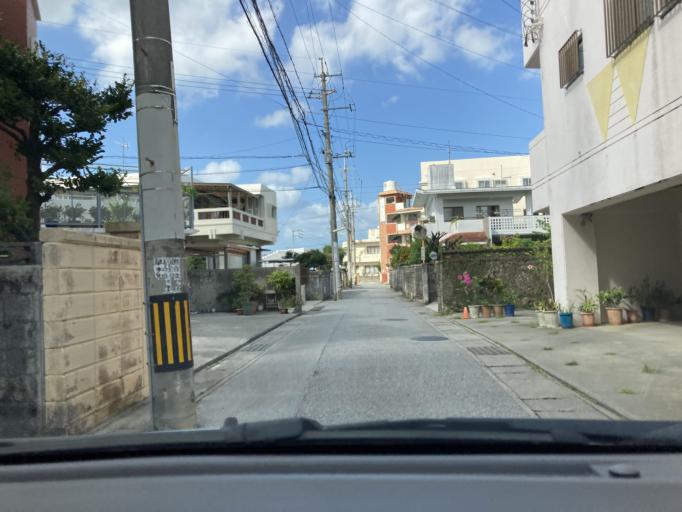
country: JP
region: Okinawa
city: Naha-shi
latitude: 26.2112
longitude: 127.7127
